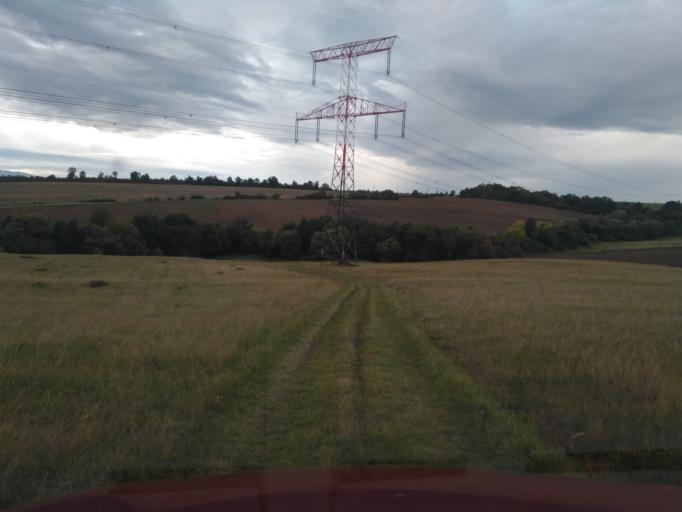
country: SK
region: Presovsky
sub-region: Okres Presov
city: Presov
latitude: 48.8968
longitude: 21.3354
